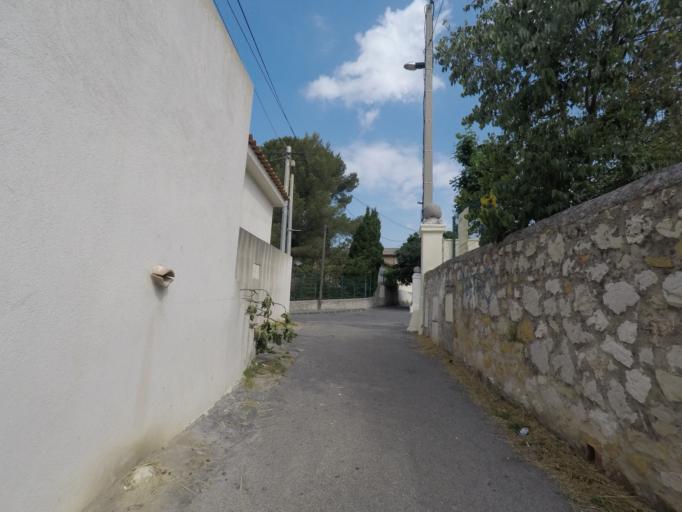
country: FR
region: Provence-Alpes-Cote d'Azur
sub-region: Departement des Bouches-du-Rhone
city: Marseille 10
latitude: 43.2623
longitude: 5.4224
